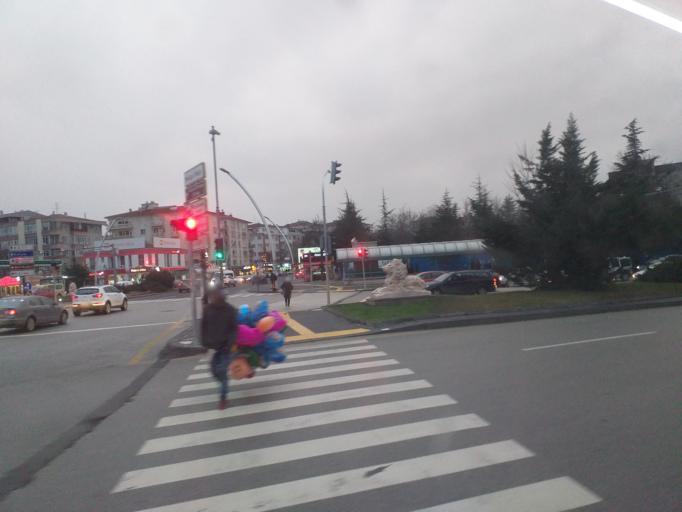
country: TR
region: Ankara
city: Ankara
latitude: 39.9331
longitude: 32.8291
